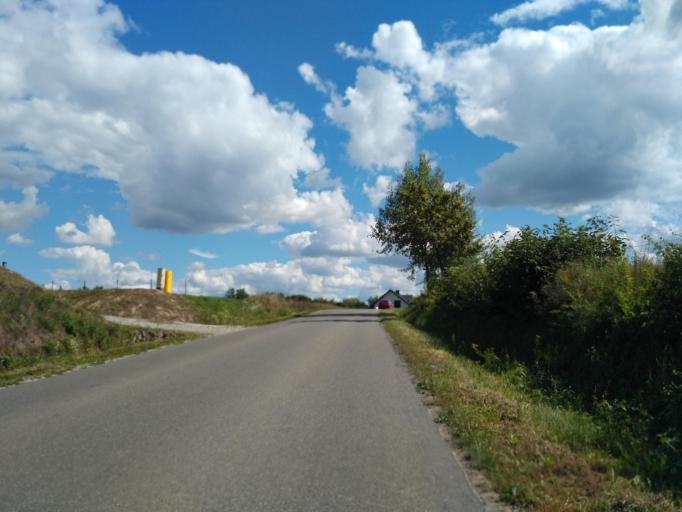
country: PL
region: Subcarpathian Voivodeship
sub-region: Powiat jasielski
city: Trzcinica
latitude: 49.7561
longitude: 21.4113
